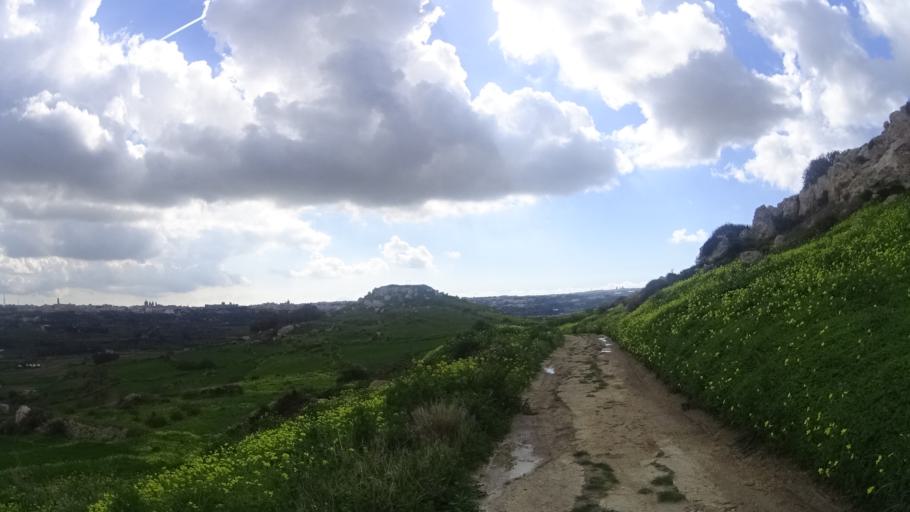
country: MT
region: L-Imtarfa
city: Imtarfa
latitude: 35.9016
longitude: 14.3842
